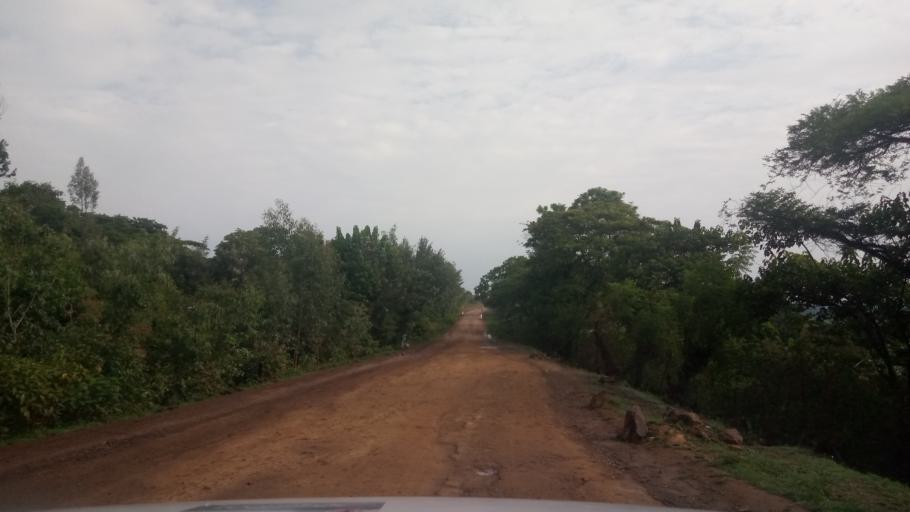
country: ET
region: Oromiya
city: Agaro
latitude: 7.8483
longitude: 36.6567
